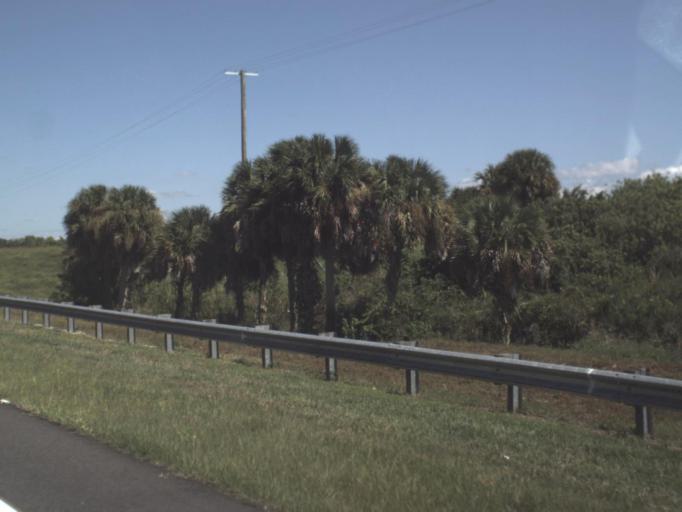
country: US
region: Florida
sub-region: Glades County
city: Buckhead Ridge
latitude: 27.0648
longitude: -80.9788
